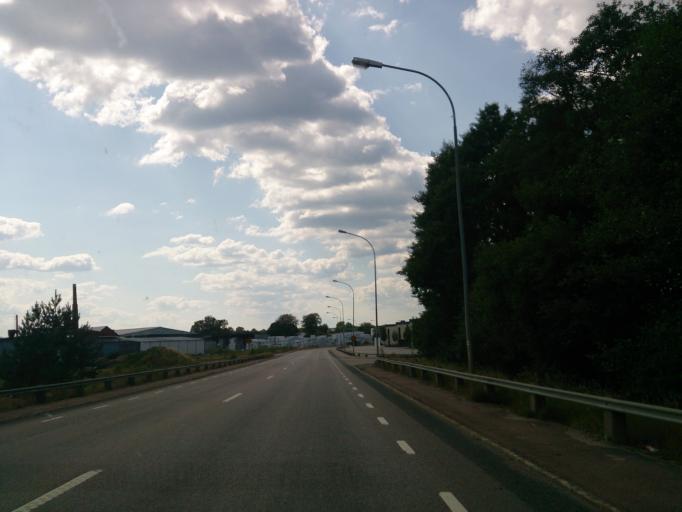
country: SE
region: Joenkoeping
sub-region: Gislaveds Kommun
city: Smalandsstenar
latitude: 57.1625
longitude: 13.4263
